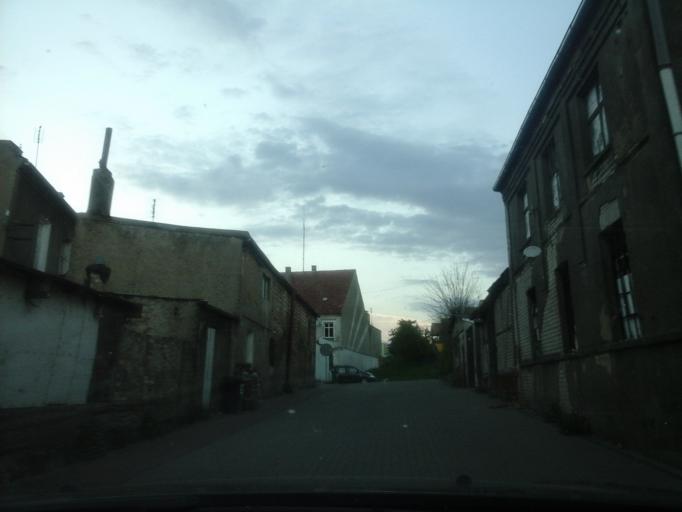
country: PL
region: West Pomeranian Voivodeship
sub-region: Powiat choszczenski
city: Pelczyce
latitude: 53.0433
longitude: 15.3050
